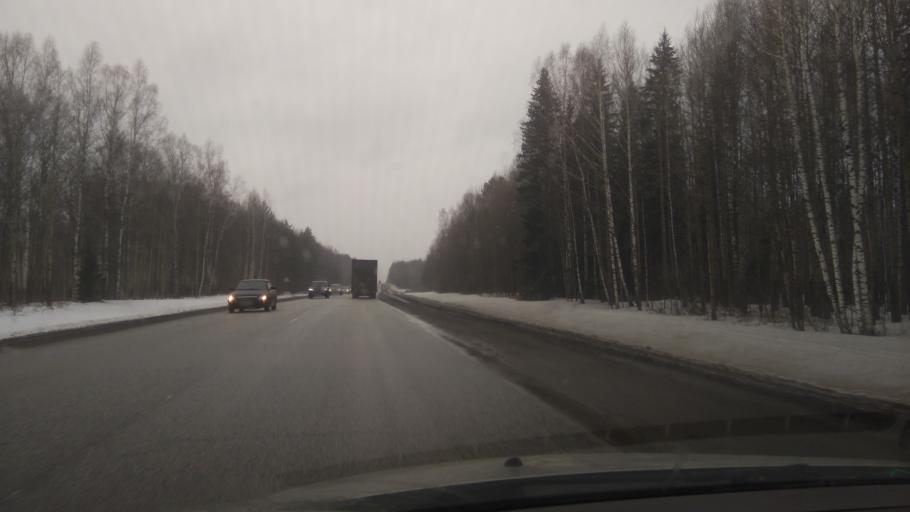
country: RU
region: Perm
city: Kungur
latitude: 57.4326
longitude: 56.8266
